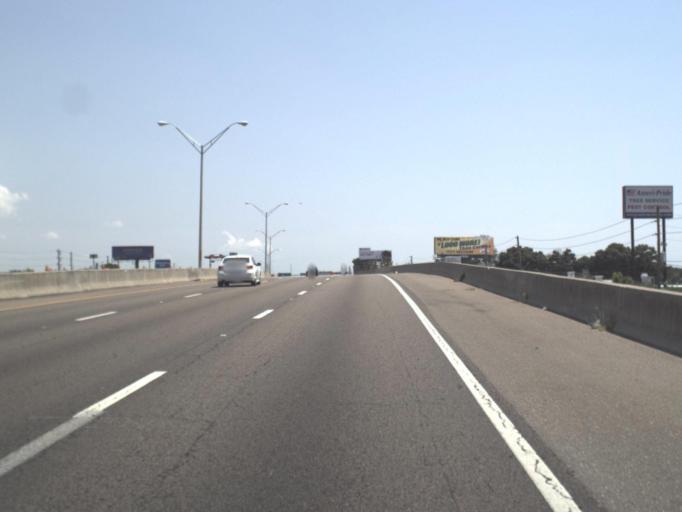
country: US
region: Florida
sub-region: Pinellas County
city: South Highpoint
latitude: 27.9249
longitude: -82.7306
